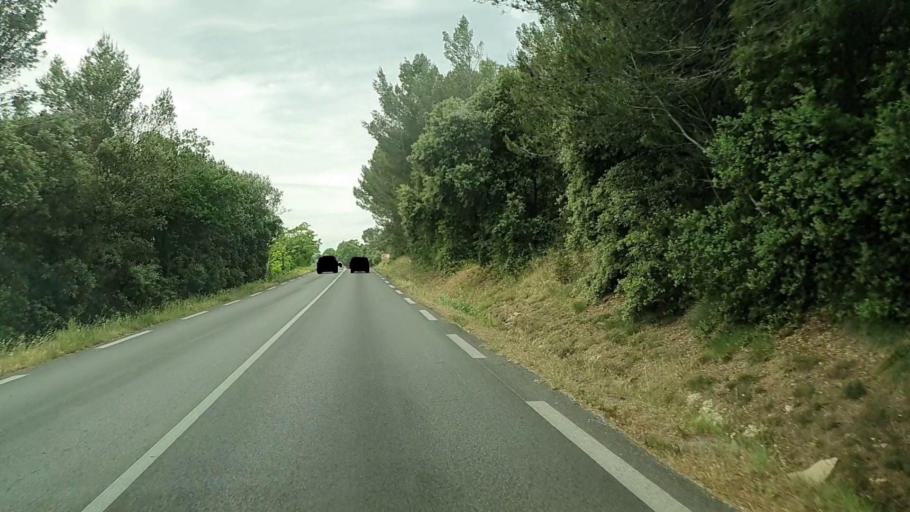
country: FR
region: Languedoc-Roussillon
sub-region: Departement du Gard
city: Tresques
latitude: 44.1107
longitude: 4.6133
